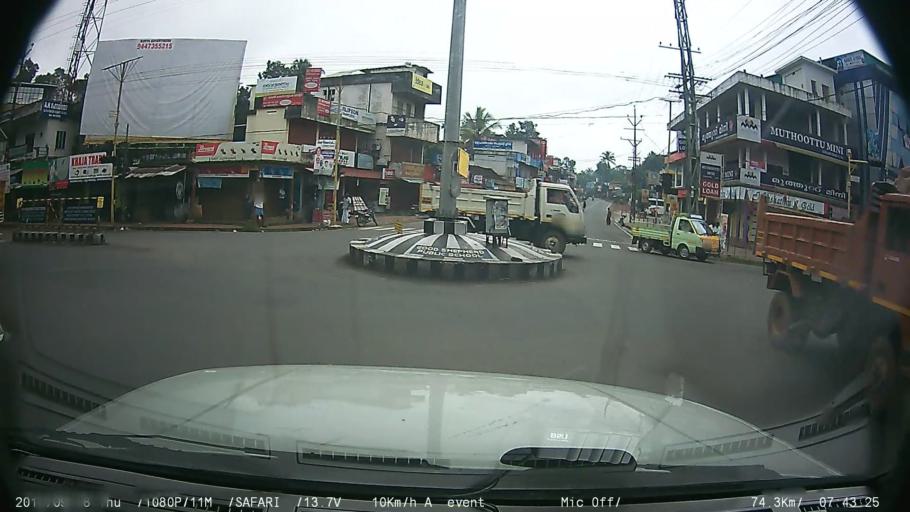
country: IN
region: Kerala
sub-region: Kottayam
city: Changanacheri
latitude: 9.4745
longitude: 76.5771
